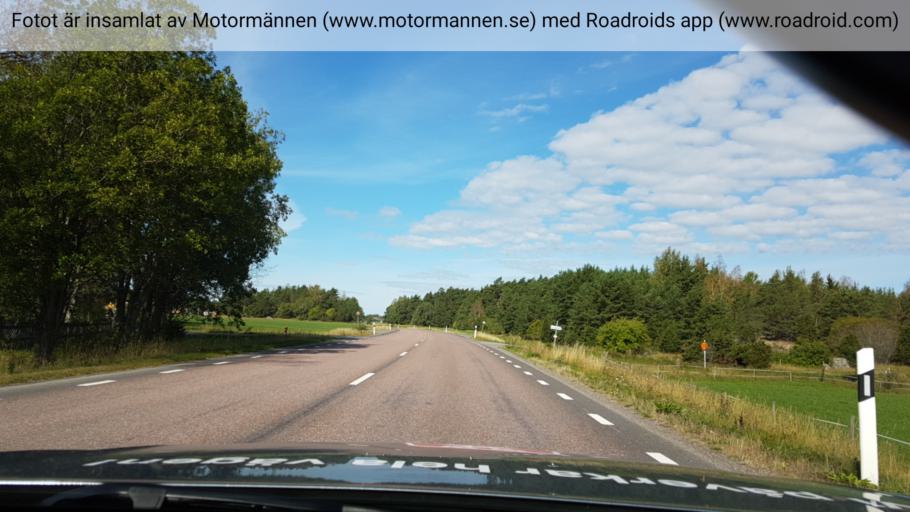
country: SE
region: Uppsala
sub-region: Osthammars Kommun
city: Bjorklinge
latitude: 59.9323
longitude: 17.4842
